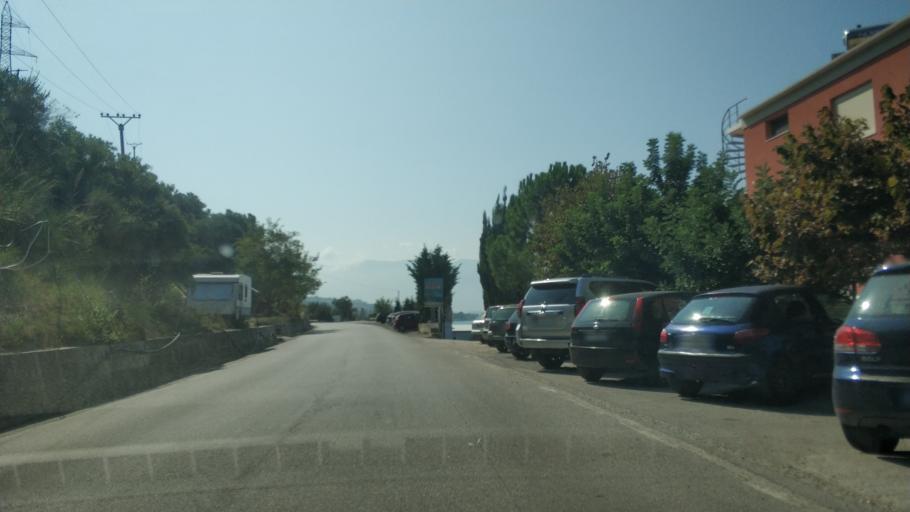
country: AL
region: Vlore
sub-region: Rrethi i Vlores
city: Orikum
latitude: 40.3937
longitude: 19.4793
